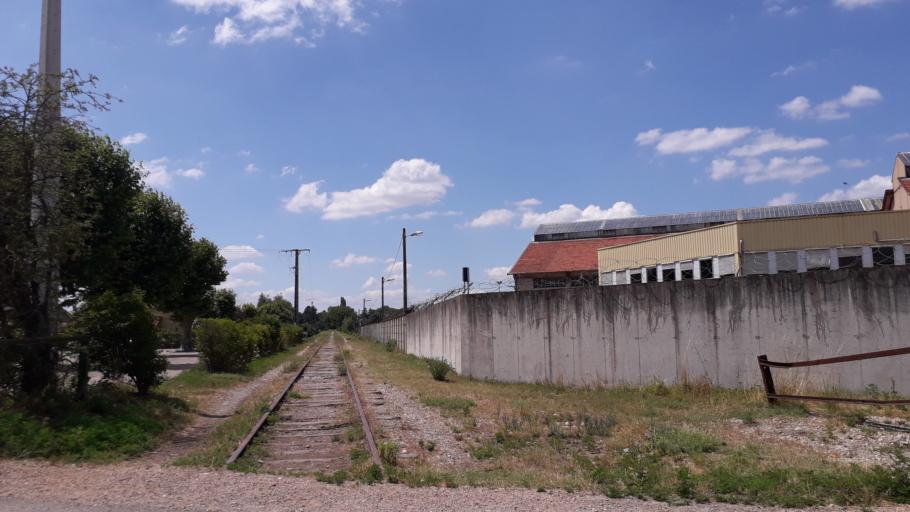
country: FR
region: Rhone-Alpes
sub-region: Departement de l'Isere
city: Charvieu-Chavagneux
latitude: 45.7470
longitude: 5.1642
